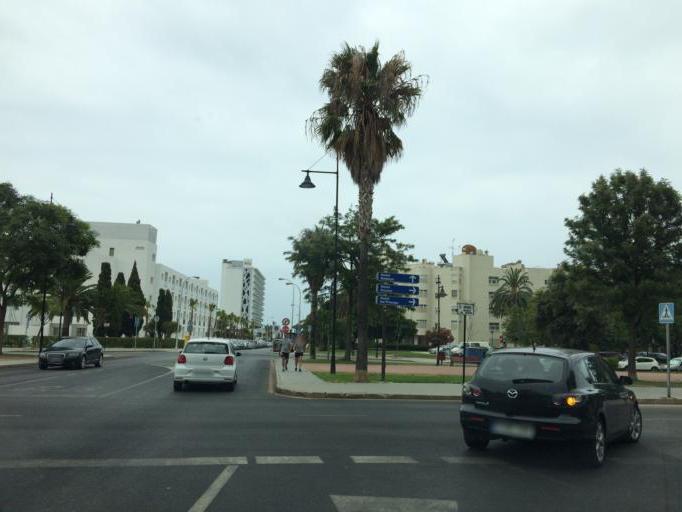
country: ES
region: Andalusia
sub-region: Provincia de Malaga
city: Torremolinos
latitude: 36.6366
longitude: -4.4902
